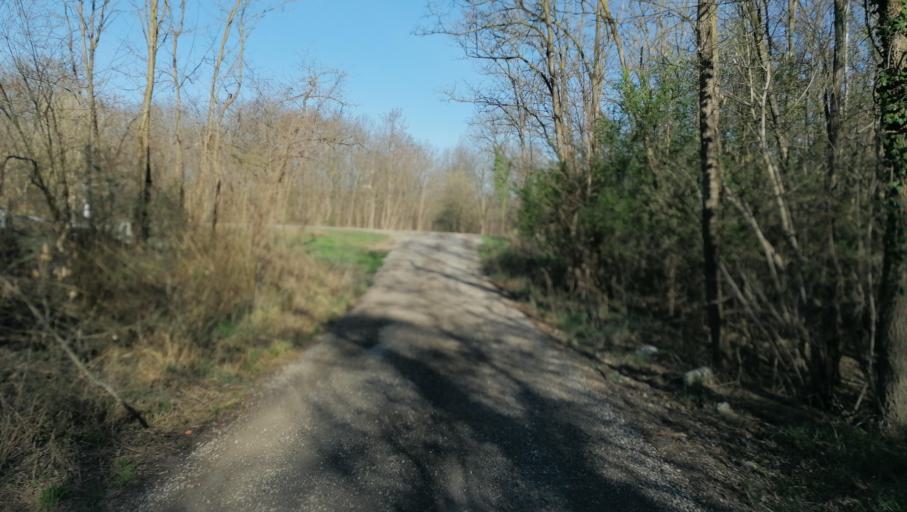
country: HU
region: Pest
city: Szentendre
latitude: 47.6650
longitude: 19.1008
